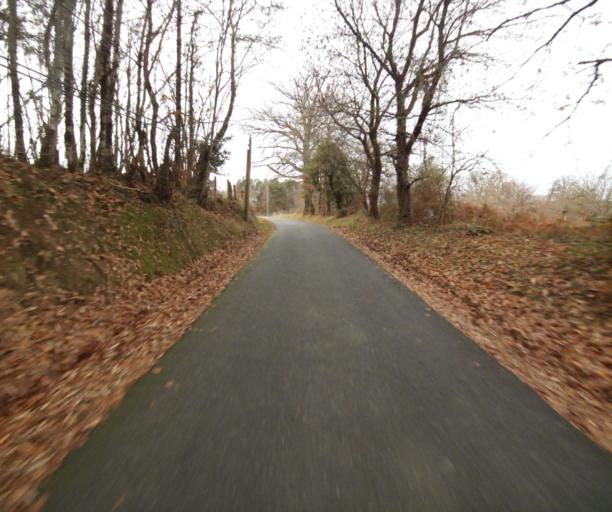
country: FR
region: Limousin
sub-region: Departement de la Correze
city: Chameyrat
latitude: 45.2350
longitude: 1.6873
